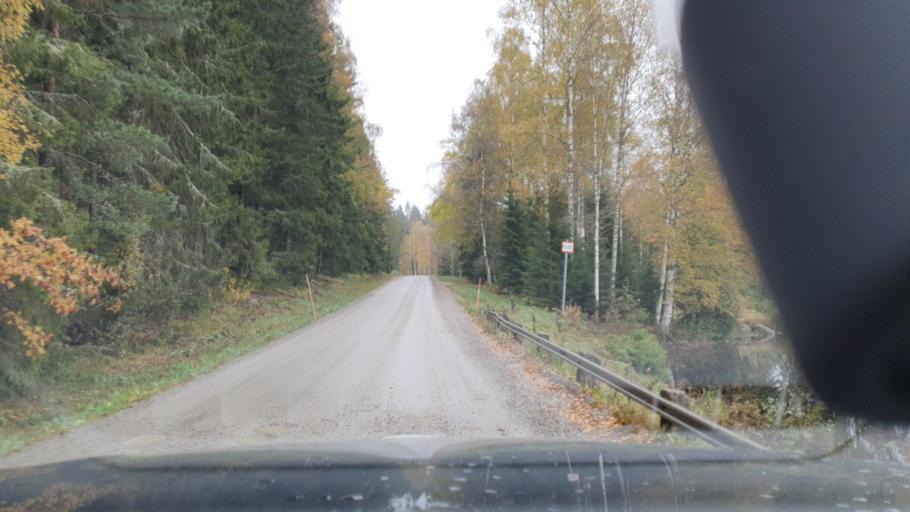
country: SE
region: Vaermland
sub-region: Arvika Kommun
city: Arvika
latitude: 59.8146
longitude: 12.7455
